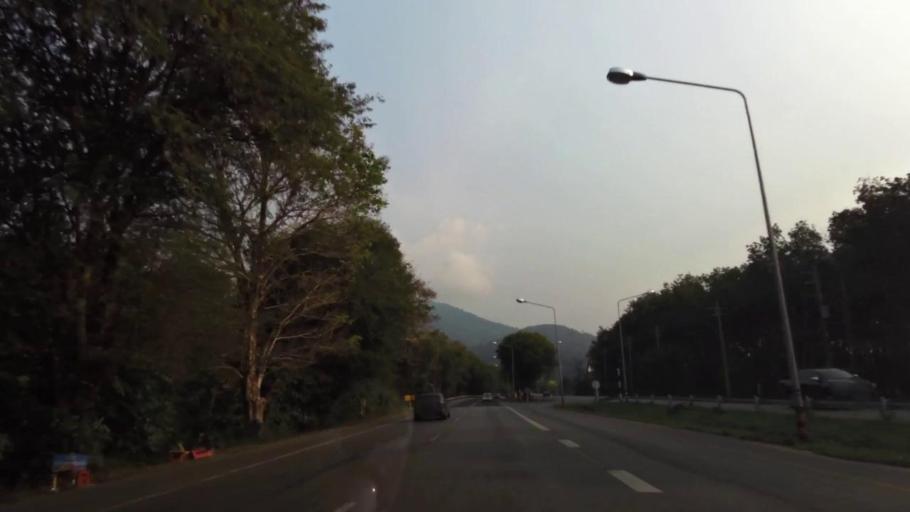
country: TH
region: Chanthaburi
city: Chanthaburi
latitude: 12.5761
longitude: 102.1608
